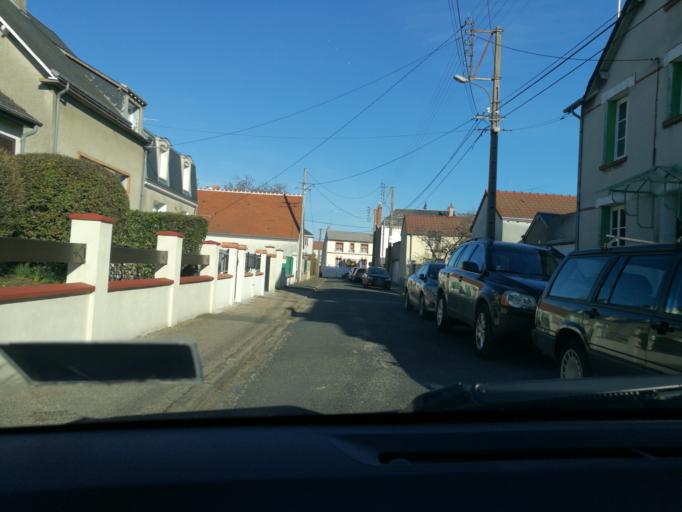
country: FR
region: Centre
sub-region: Departement du Loiret
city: Orleans
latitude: 47.9129
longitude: 1.8912
